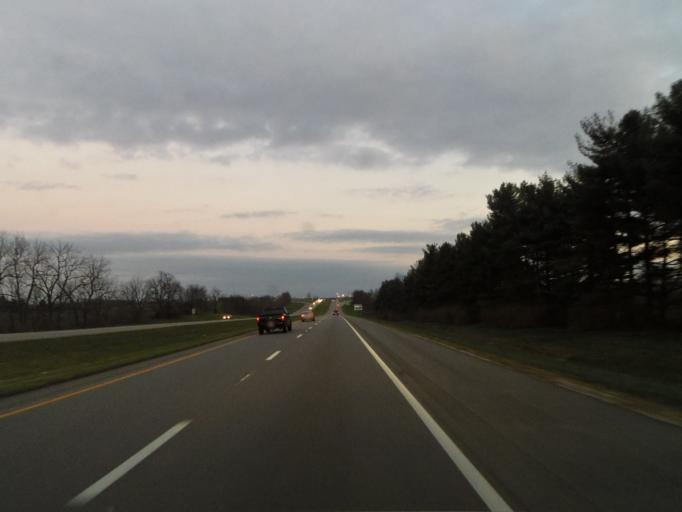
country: US
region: Kentucky
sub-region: Woodford County
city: Midway
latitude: 38.1618
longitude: -84.6240
